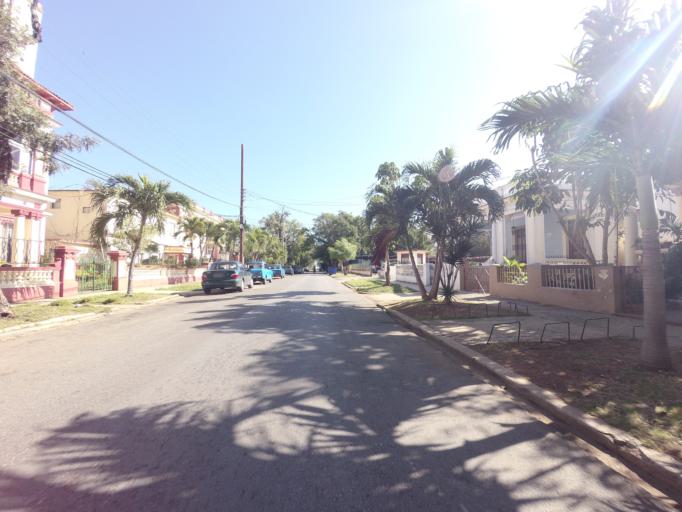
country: CU
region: La Habana
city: Havana
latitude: 23.1414
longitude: -82.3904
